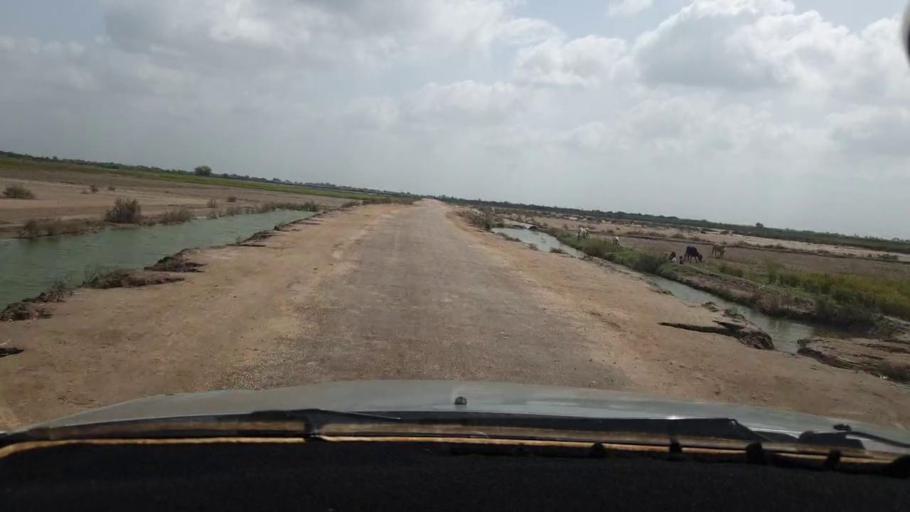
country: PK
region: Sindh
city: Tando Bago
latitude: 24.7207
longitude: 69.1491
